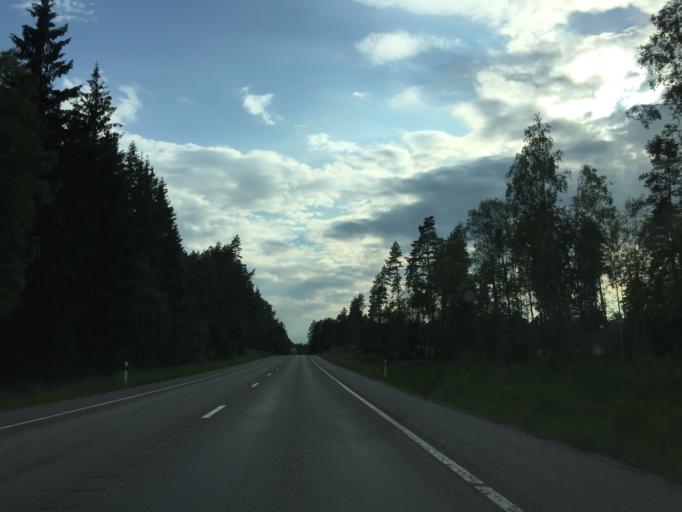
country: SE
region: OErebro
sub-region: Lindesbergs Kommun
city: Fellingsbro
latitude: 59.3468
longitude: 15.6262
